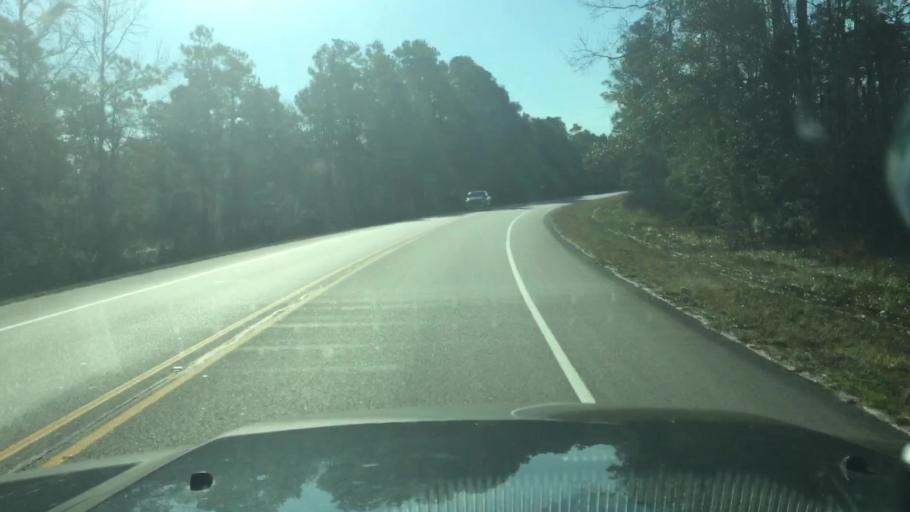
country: US
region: Texas
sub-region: Montgomery County
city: Porter Heights
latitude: 30.2243
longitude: -95.3612
